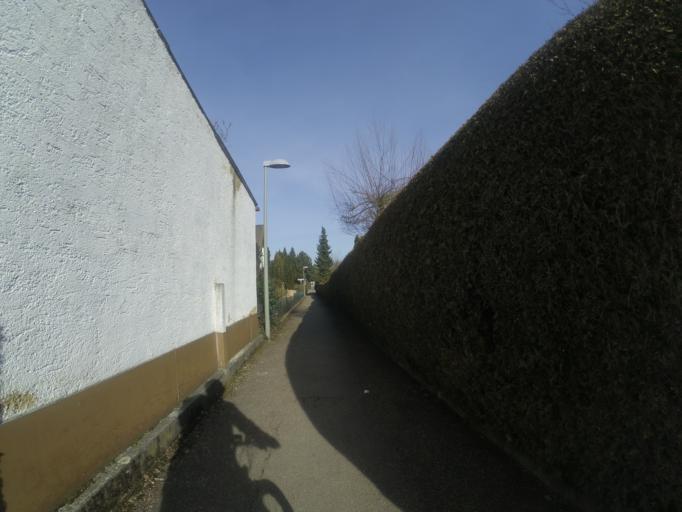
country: DE
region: Baden-Wuerttemberg
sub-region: Tuebingen Region
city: Beimerstetten
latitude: 48.4483
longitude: 9.9876
